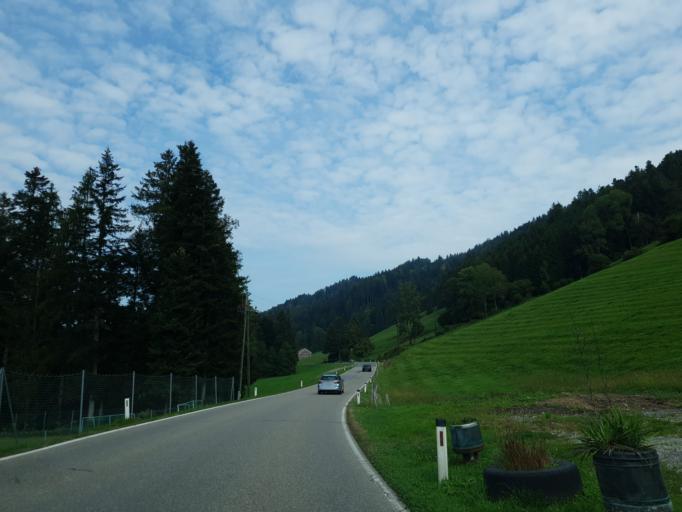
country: AT
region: Vorarlberg
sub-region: Politischer Bezirk Bregenz
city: Doren
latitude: 47.4926
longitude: 9.8537
